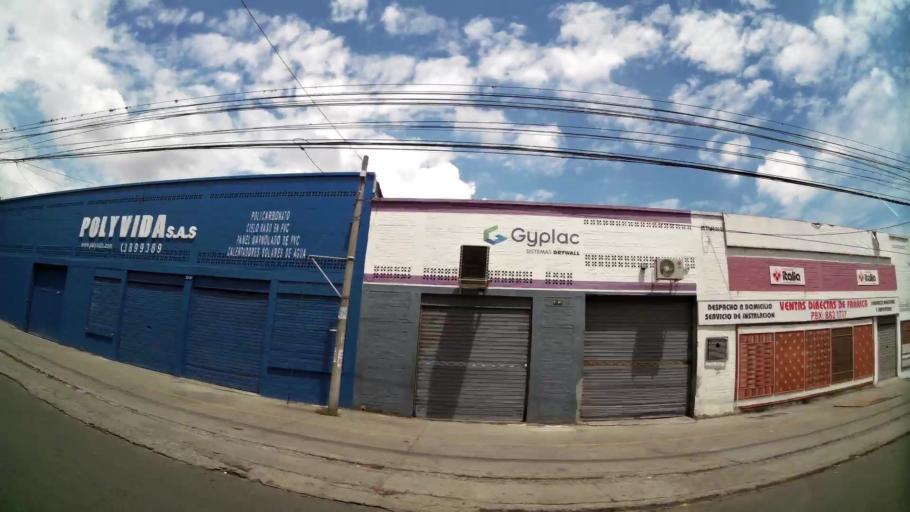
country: CO
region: Valle del Cauca
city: Cali
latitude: 3.4561
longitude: -76.5226
